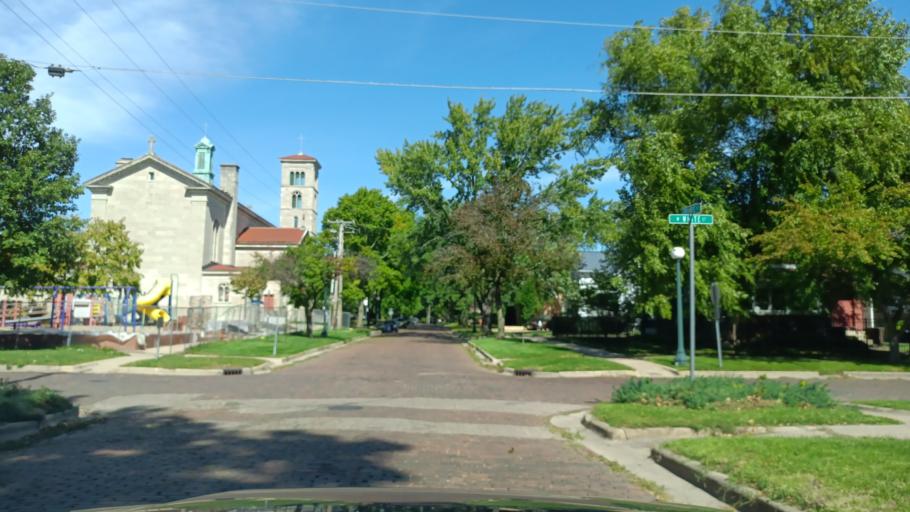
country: US
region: Illinois
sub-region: Champaign County
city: Champaign
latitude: 40.1141
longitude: -88.2485
